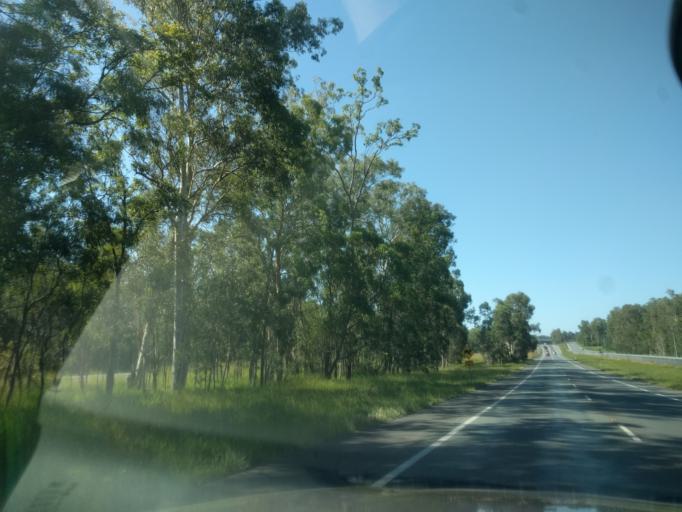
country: AU
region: Queensland
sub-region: Logan
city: Park Ridge South
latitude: -27.7330
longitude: 153.0285
